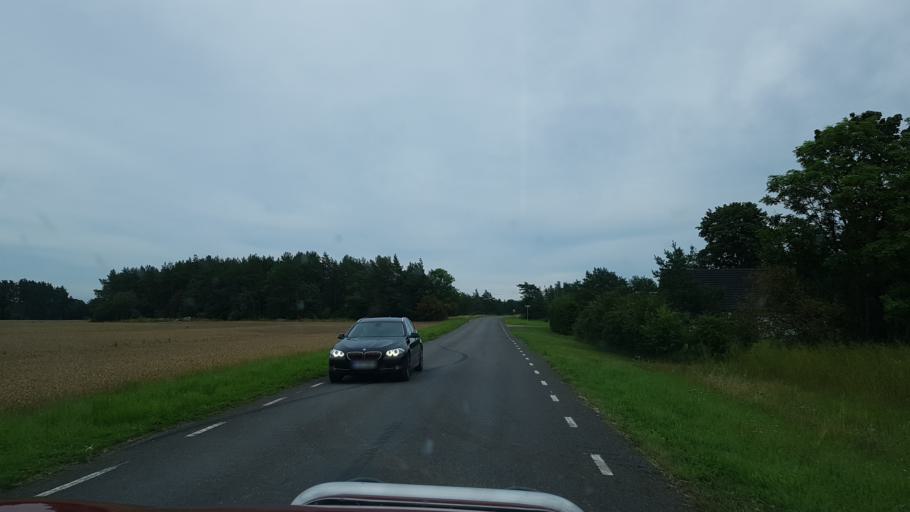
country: EE
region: Laeaene
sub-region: Ridala Parish
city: Uuemoisa
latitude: 58.9355
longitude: 23.7400
